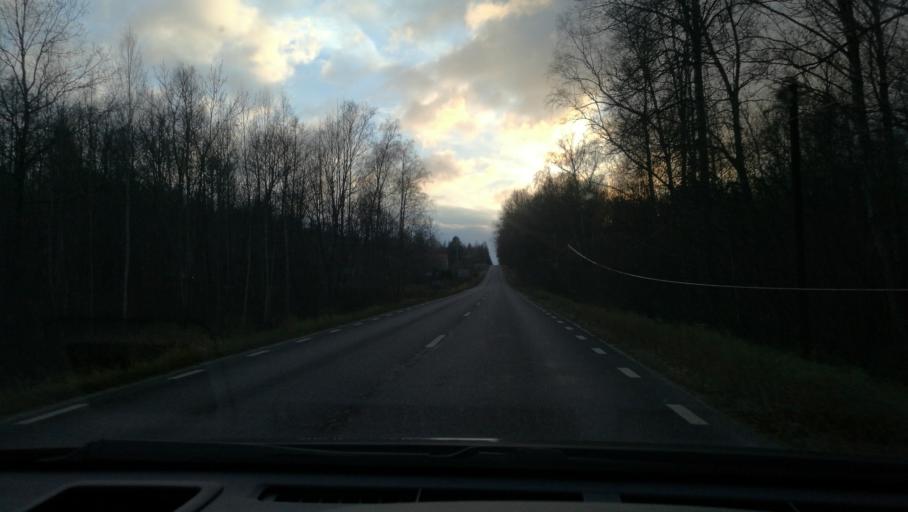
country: SE
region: Soedermanland
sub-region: Vingakers Kommun
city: Vingaker
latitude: 59.1624
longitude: 15.9375
